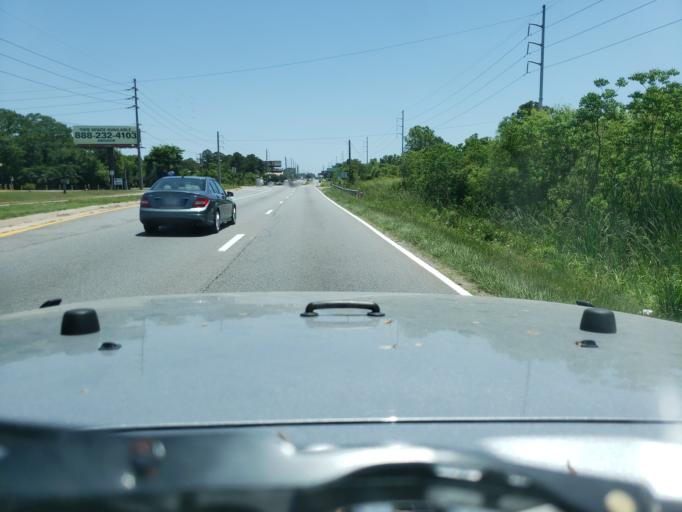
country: US
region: Georgia
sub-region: Chatham County
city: Savannah
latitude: 32.0724
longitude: -81.0690
